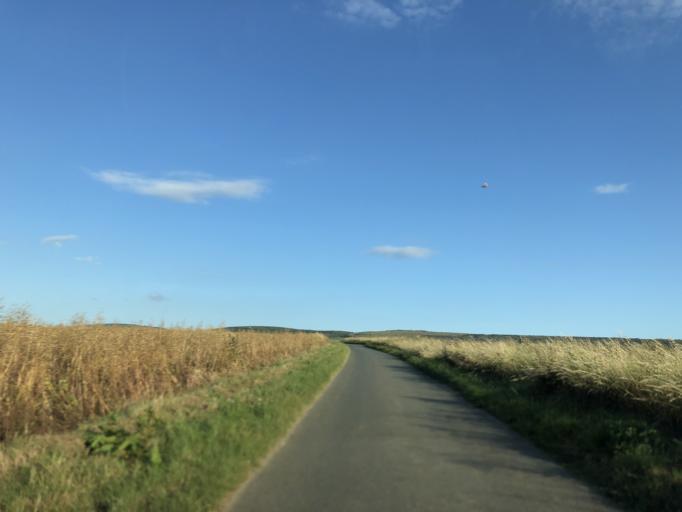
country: GB
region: England
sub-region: Isle of Wight
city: Yarmouth
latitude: 50.6865
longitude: -1.4704
